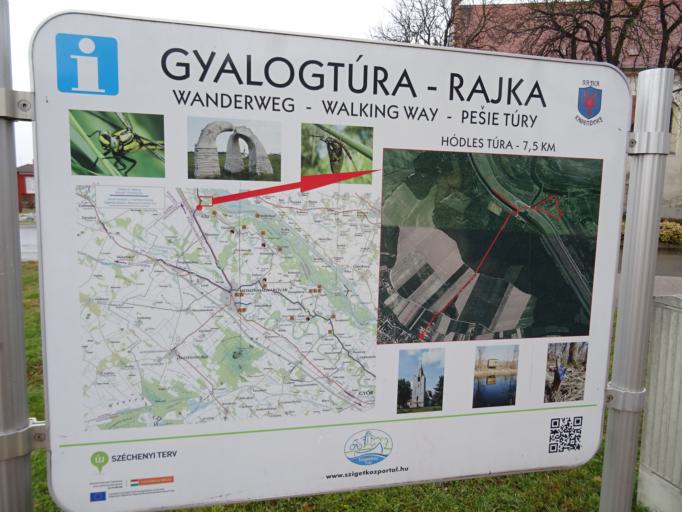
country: HU
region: Gyor-Moson-Sopron
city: Rajka
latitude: 47.9990
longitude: 17.2010
